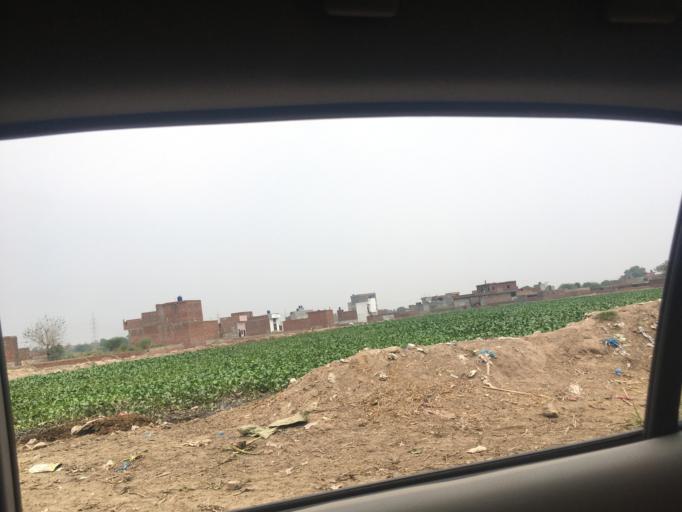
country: PK
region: Punjab
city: Lahore
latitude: 31.6210
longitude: 74.3468
